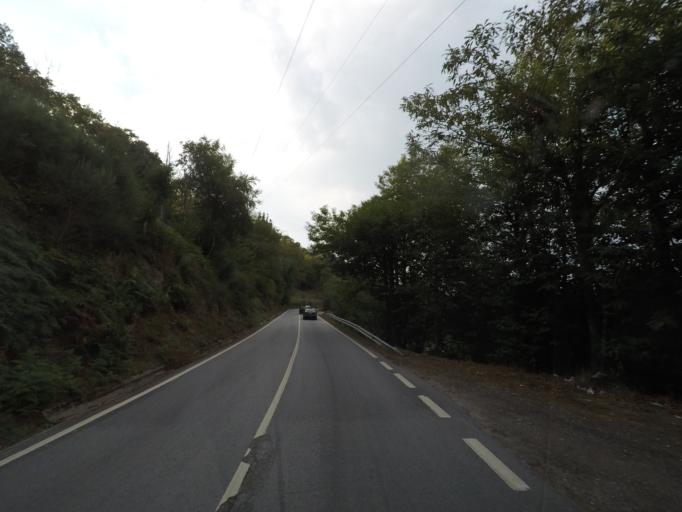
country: PT
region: Porto
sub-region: Baiao
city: Valadares
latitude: 41.1932
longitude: -7.9467
